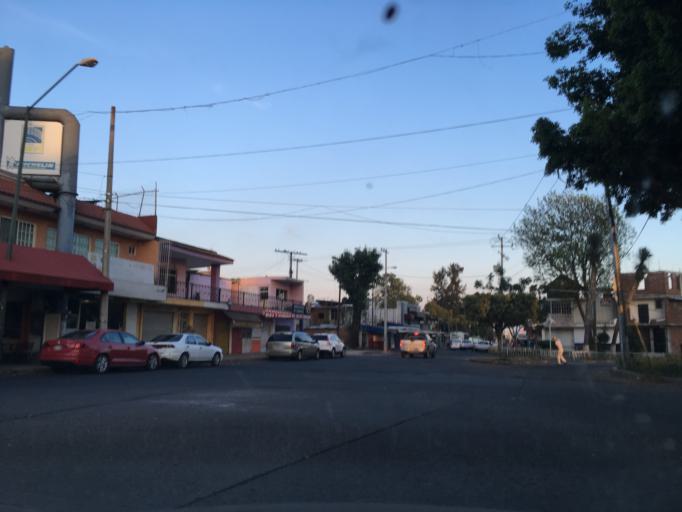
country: MX
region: Michoacan
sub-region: Uruapan
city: Uruapan
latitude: 19.4180
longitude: -102.0505
